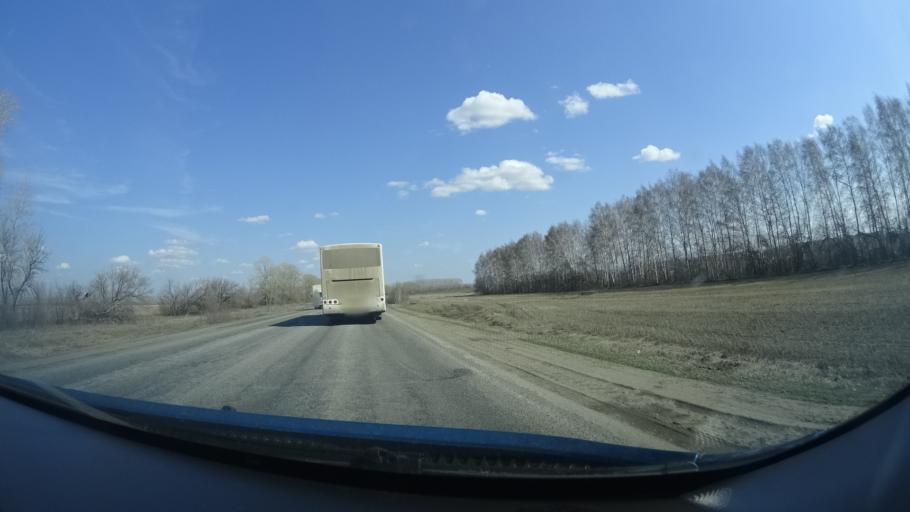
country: RU
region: Bashkortostan
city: Buzdyak
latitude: 54.6174
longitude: 54.3644
